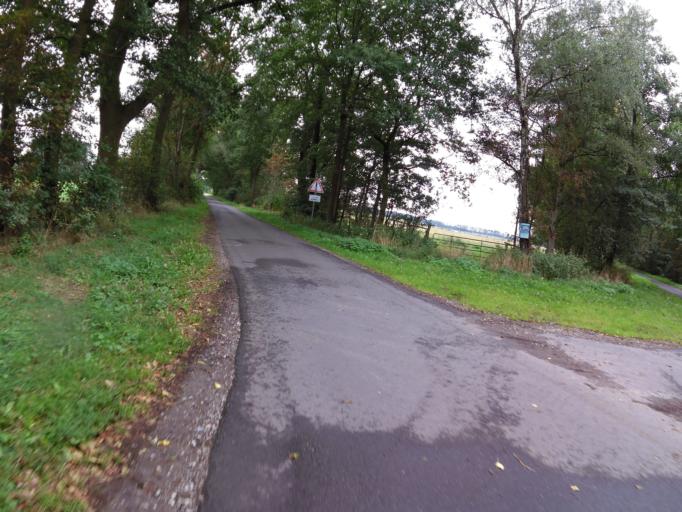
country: DE
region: Lower Saxony
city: Scheessel
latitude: 53.1587
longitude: 9.4556
